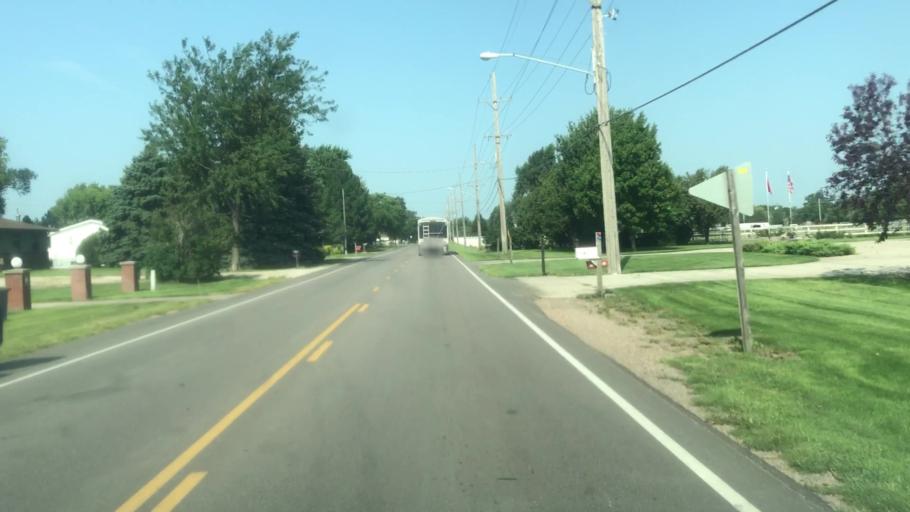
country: US
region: Nebraska
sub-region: Hall County
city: Grand Island
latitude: 40.9456
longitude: -98.3354
